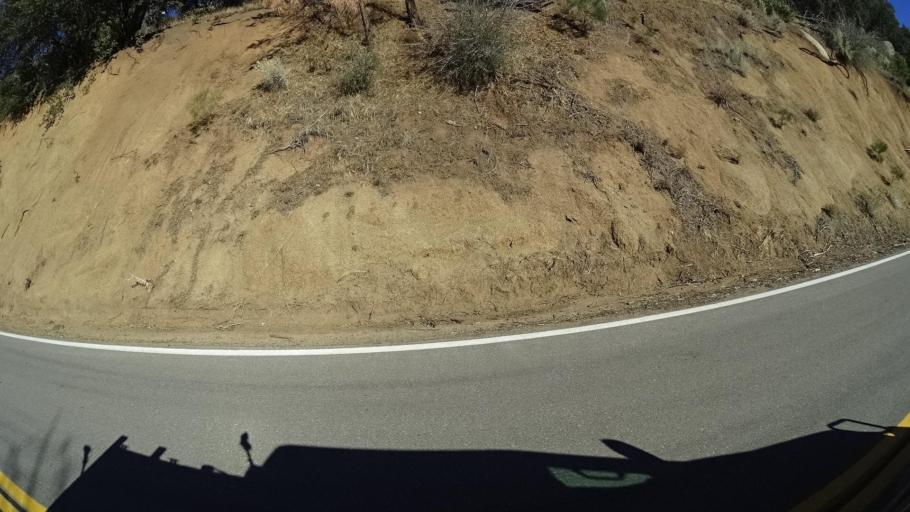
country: US
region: California
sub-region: Kern County
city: Alta Sierra
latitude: 35.7473
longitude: -118.5886
